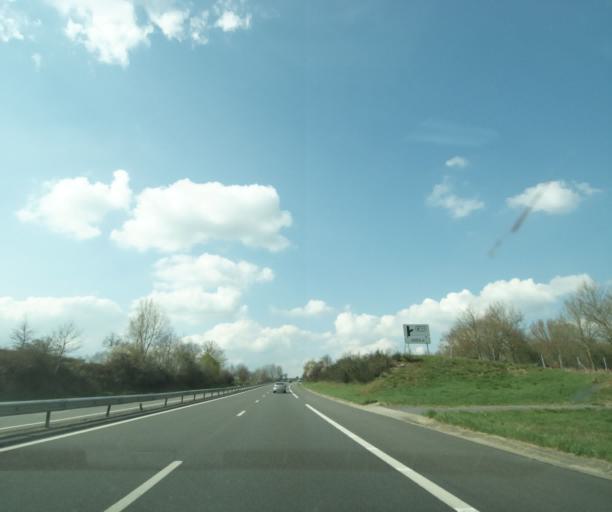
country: FR
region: Auvergne
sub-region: Departement de l'Allier
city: Montmarault
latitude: 46.3162
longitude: 2.9899
